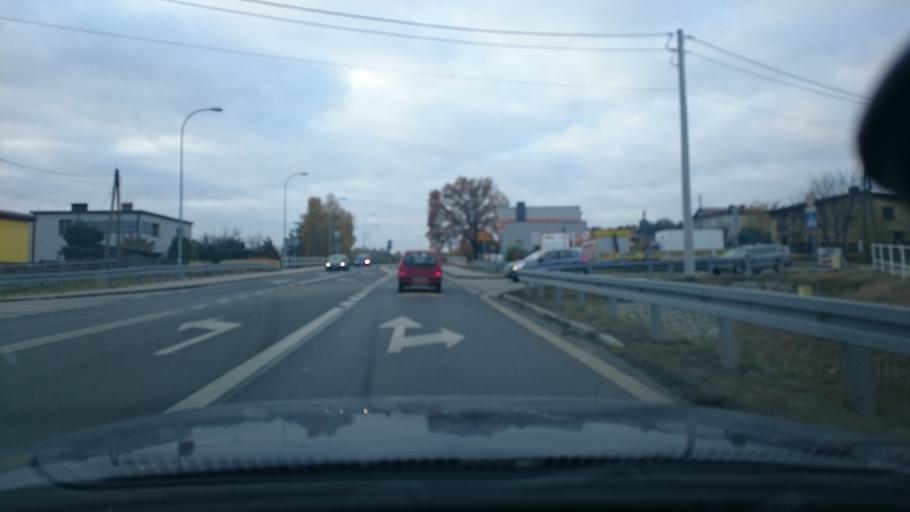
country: PL
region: Silesian Voivodeship
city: Zebrzydowice
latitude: 50.1133
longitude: 18.5149
